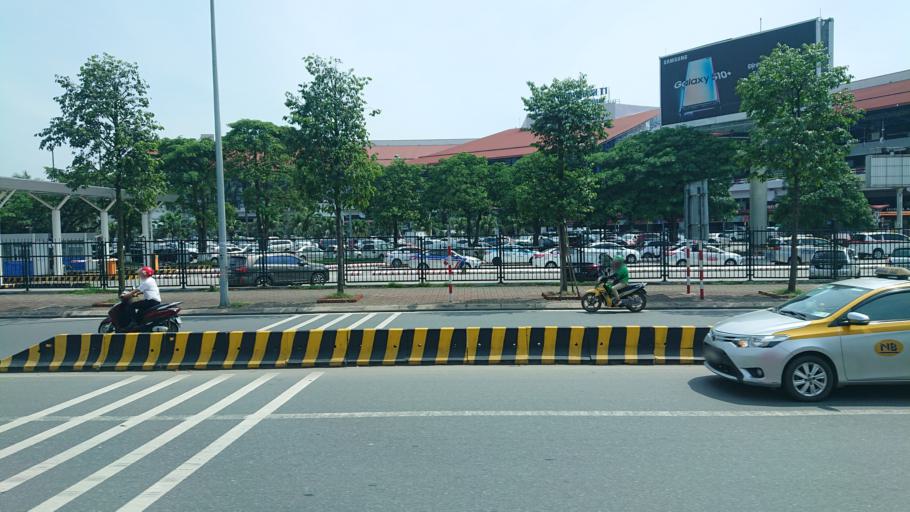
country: VN
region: Ha Noi
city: Soc Son
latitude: 21.2131
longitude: 105.8028
